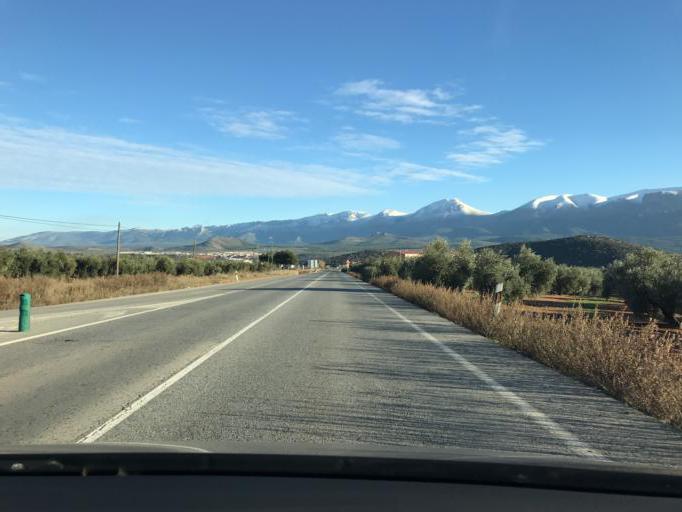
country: ES
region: Andalusia
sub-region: Provincia de Granada
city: Iznalloz
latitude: 37.4029
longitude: -3.5587
